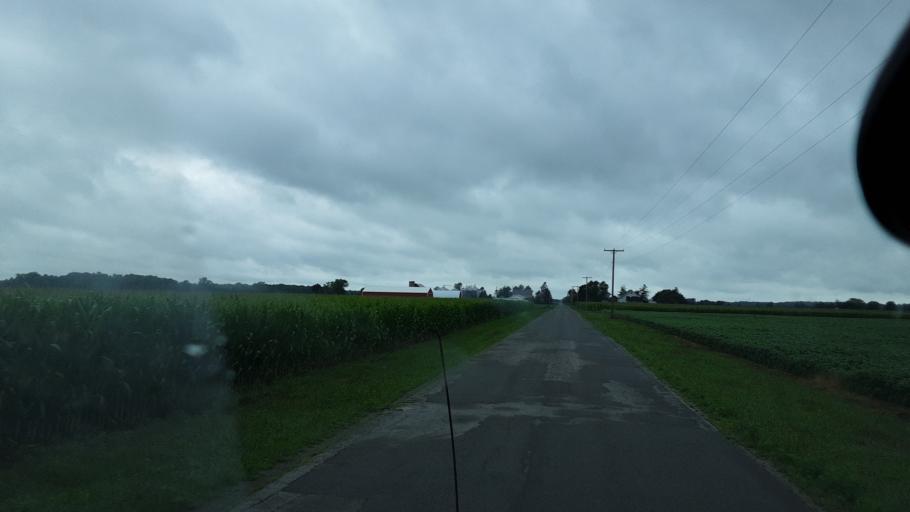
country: US
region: Ohio
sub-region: Van Wert County
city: Convoy
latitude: 40.8223
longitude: -84.6815
